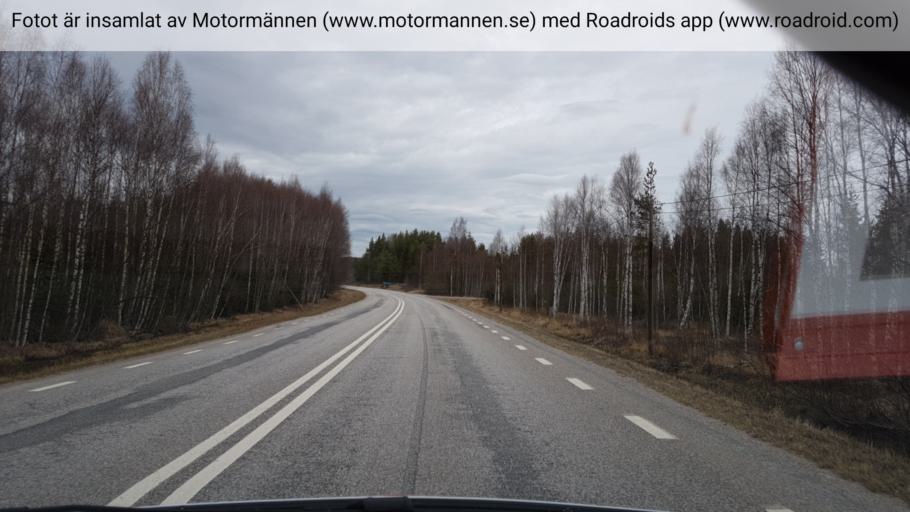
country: SE
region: Vaesternorrland
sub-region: Solleftea Kommun
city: As
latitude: 63.4982
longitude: 16.8652
